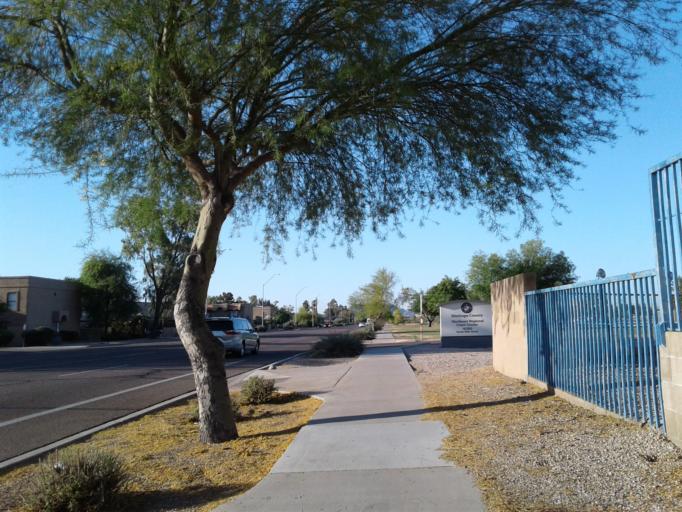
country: US
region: Arizona
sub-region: Maricopa County
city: Paradise Valley
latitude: 33.6544
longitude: -111.9965
